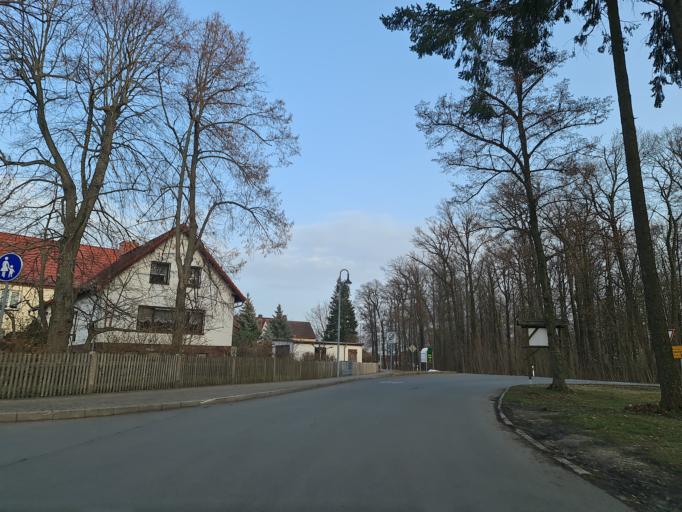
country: DE
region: Thuringia
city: Tautenhain
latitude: 50.9216
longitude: 11.9151
